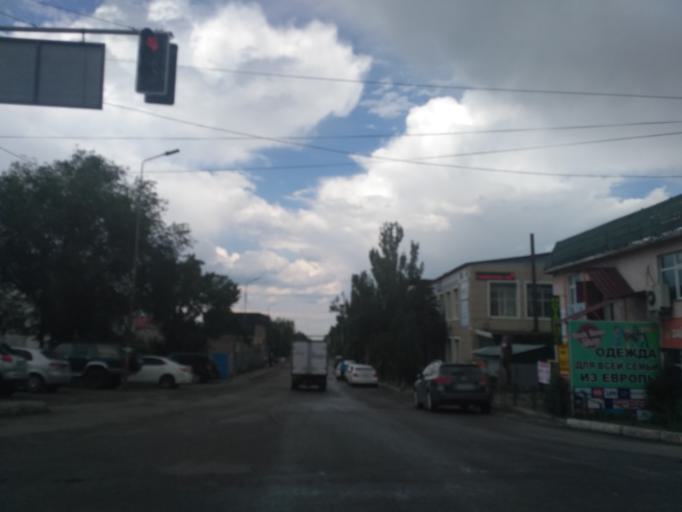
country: KZ
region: Almaty Oblysy
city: Burunday
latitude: 43.2014
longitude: 76.6274
